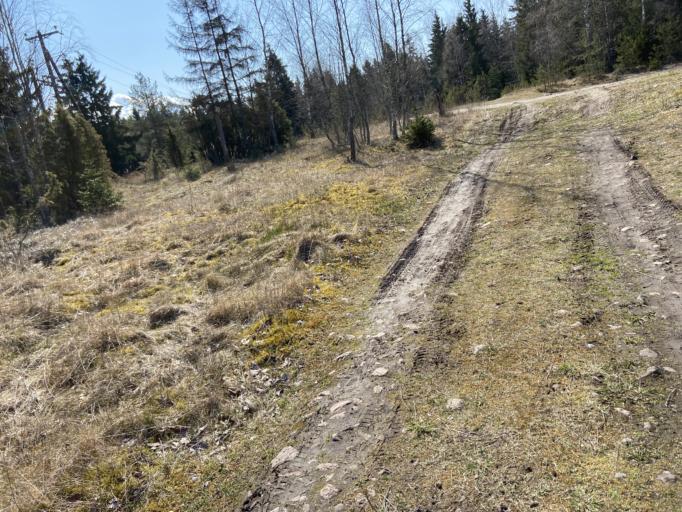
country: EE
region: Harju
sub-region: Kuusalu vald
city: Kuusalu
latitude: 59.6457
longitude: 25.5010
